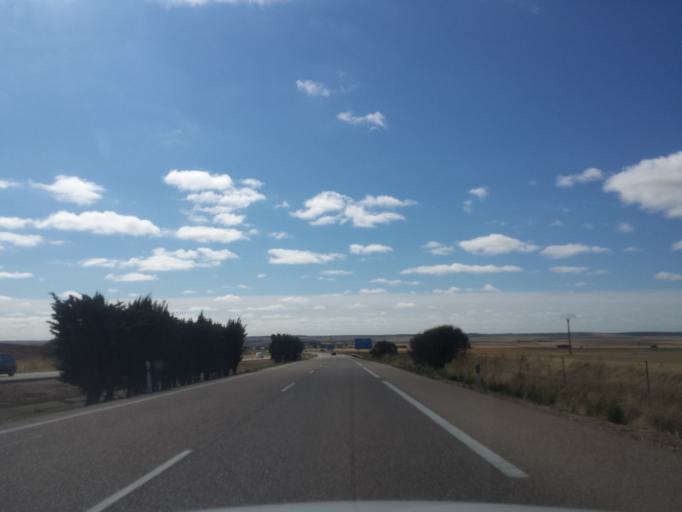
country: ES
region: Castille and Leon
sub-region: Provincia de Zamora
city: Cerecinos de Campos
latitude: 41.8796
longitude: -5.4533
